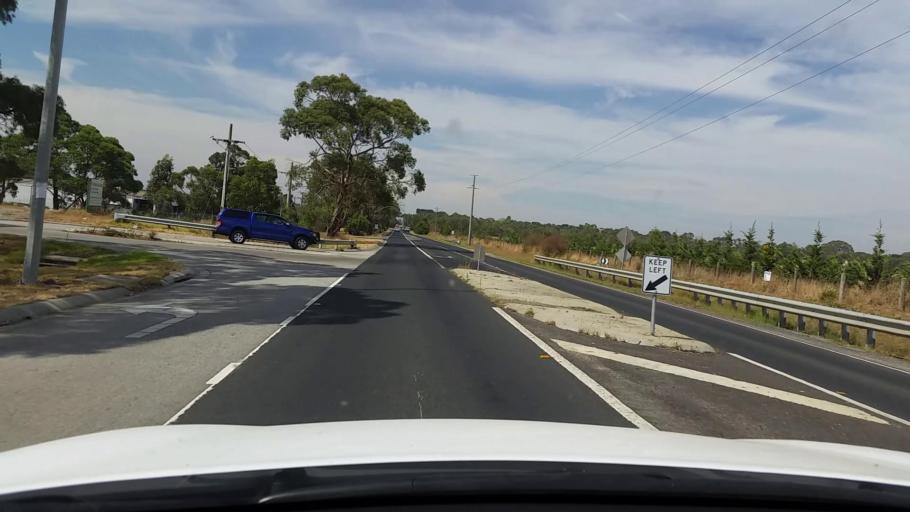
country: AU
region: Victoria
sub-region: Mornington Peninsula
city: Hastings
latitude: -38.2856
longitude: 145.1836
